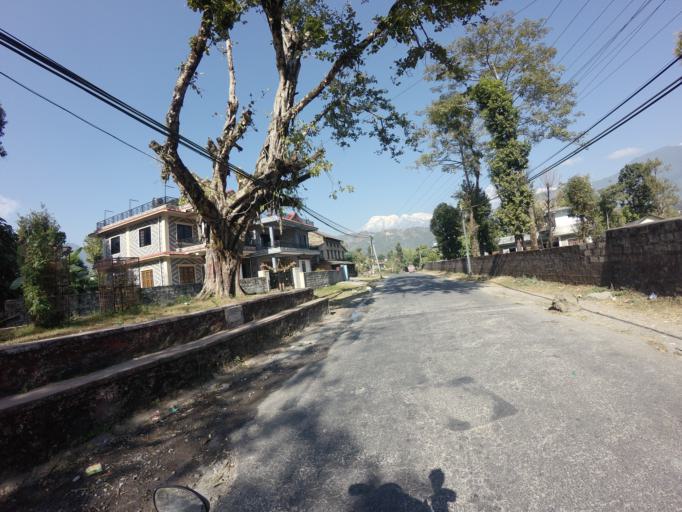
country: NP
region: Western Region
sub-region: Gandaki Zone
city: Pokhara
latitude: 28.2567
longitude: 83.9819
